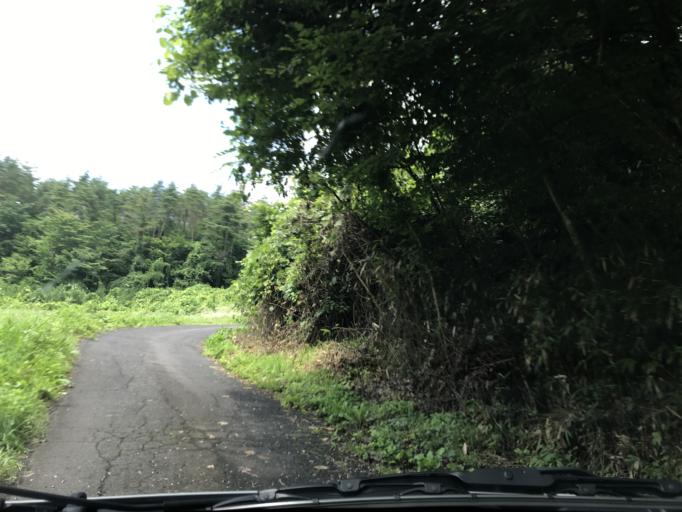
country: JP
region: Iwate
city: Mizusawa
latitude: 39.0575
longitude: 141.3816
